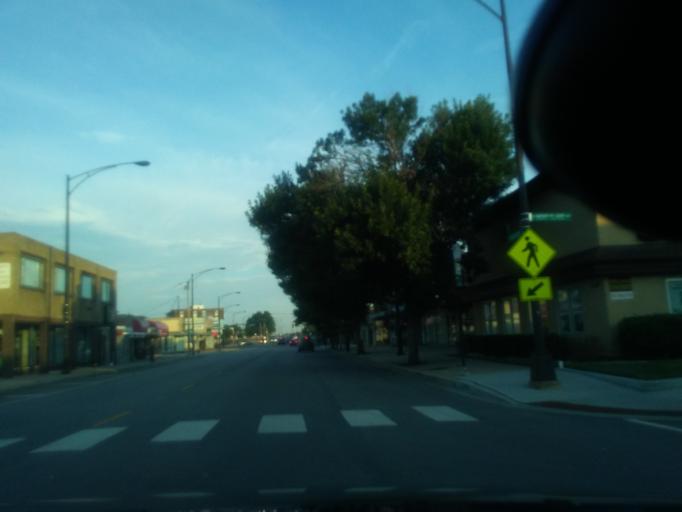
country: US
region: Illinois
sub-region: Cook County
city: Harwood Heights
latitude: 41.9806
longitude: -87.8048
